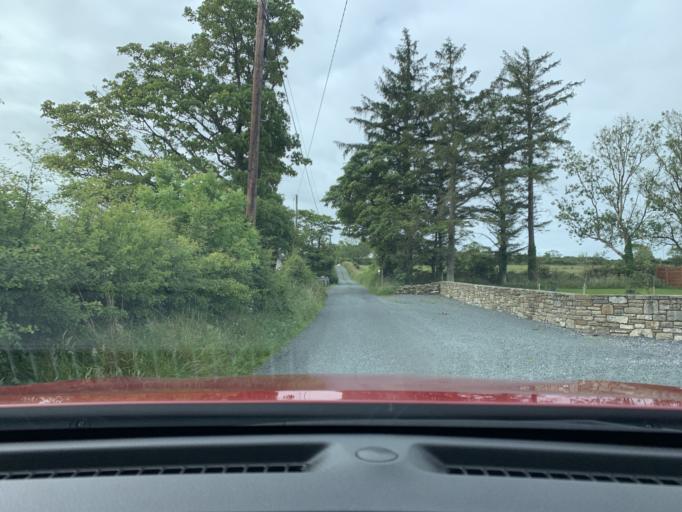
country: IE
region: Connaught
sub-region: Sligo
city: Sligo
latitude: 54.3878
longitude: -8.5221
